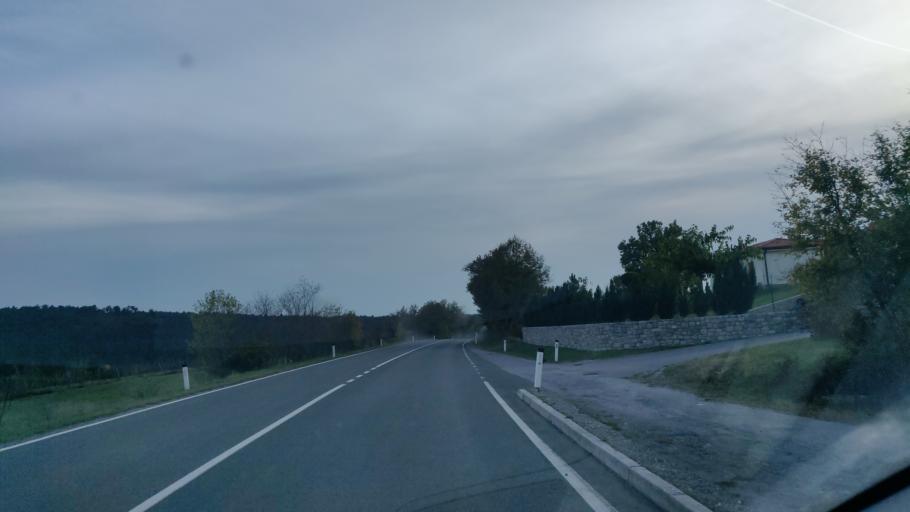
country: SI
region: Ajdovscina
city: Lokavec
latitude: 45.8126
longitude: 13.8496
